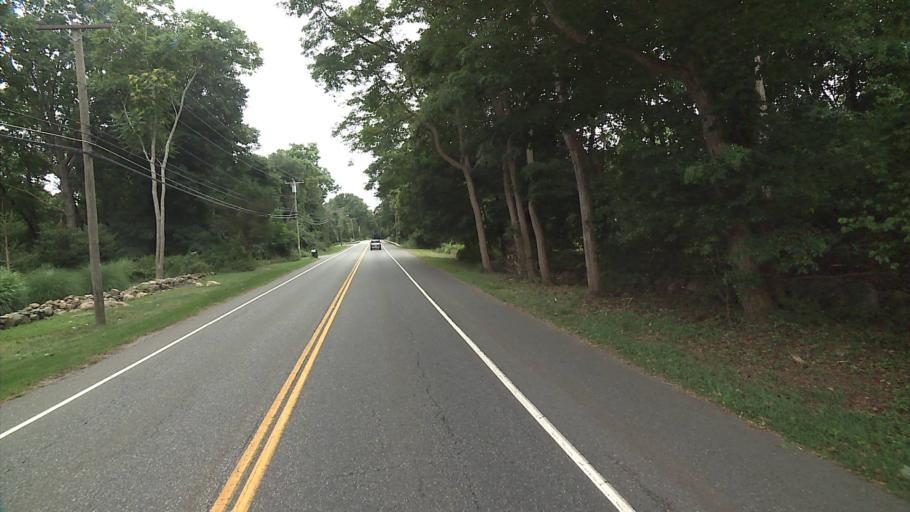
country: US
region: Connecticut
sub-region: Middlesex County
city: Old Saybrook Center
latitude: 41.2875
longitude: -72.2947
